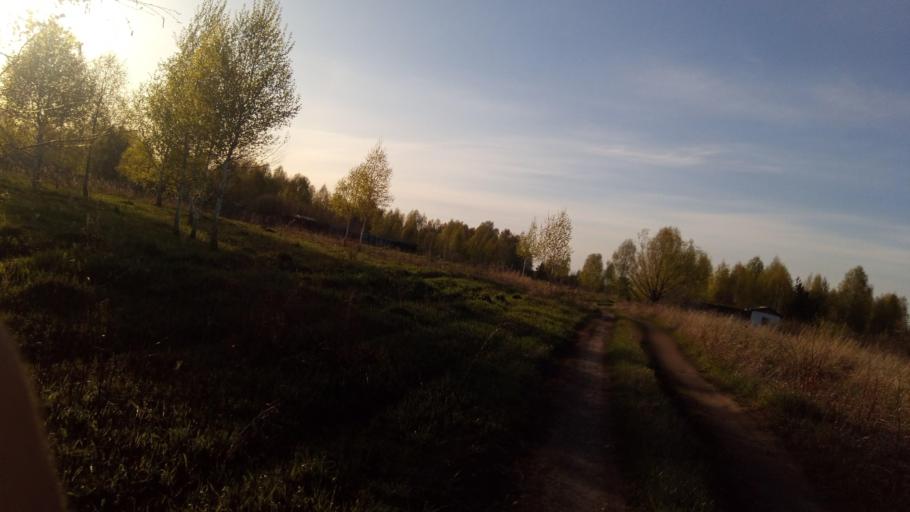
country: RU
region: Chelyabinsk
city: Timiryazevskiy
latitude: 54.9906
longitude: 60.8520
